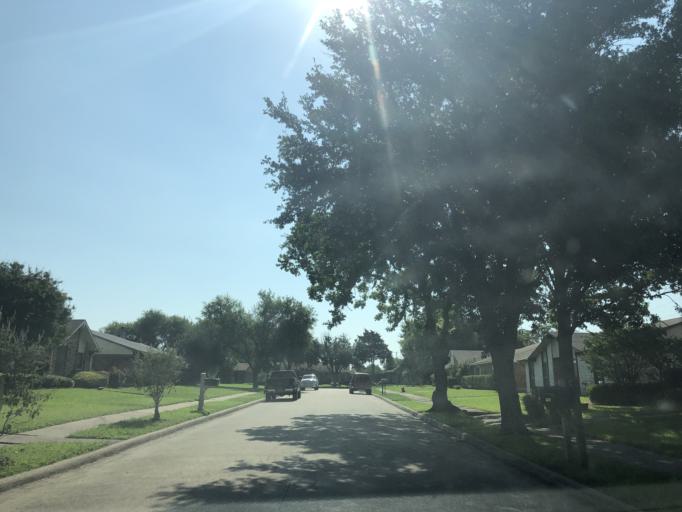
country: US
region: Texas
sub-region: Dallas County
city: Sunnyvale
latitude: 32.8206
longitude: -96.5988
